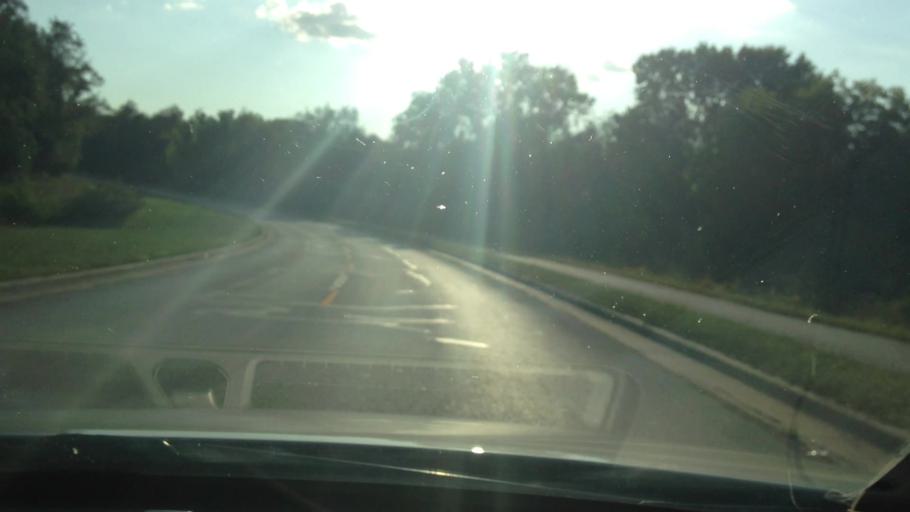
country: US
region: Missouri
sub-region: Jackson County
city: Grandview
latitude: 38.9011
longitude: -94.5159
